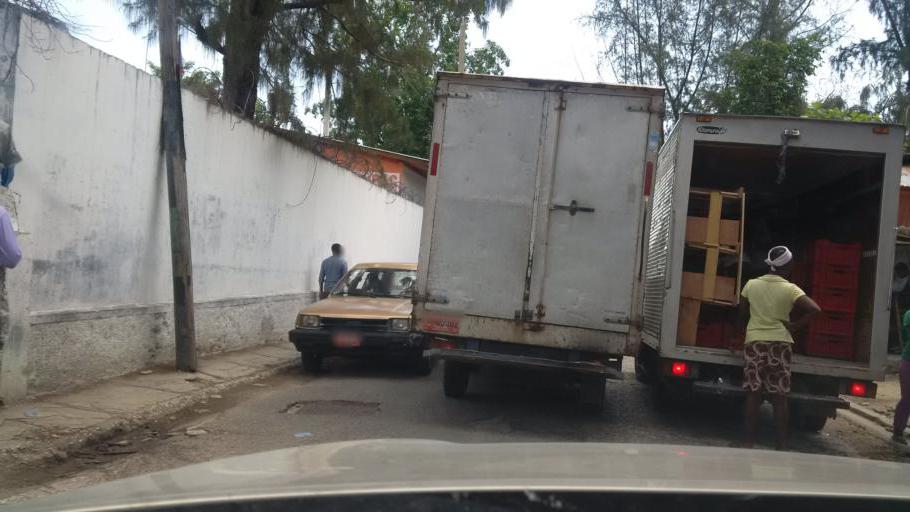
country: HT
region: Ouest
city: Port-au-Prince
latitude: 18.5325
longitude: -72.3287
